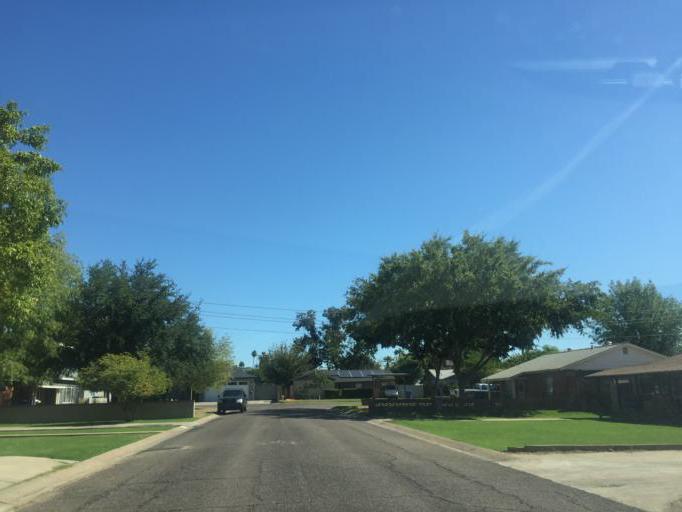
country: US
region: Arizona
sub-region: Maricopa County
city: Phoenix
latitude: 33.5364
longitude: -112.0614
